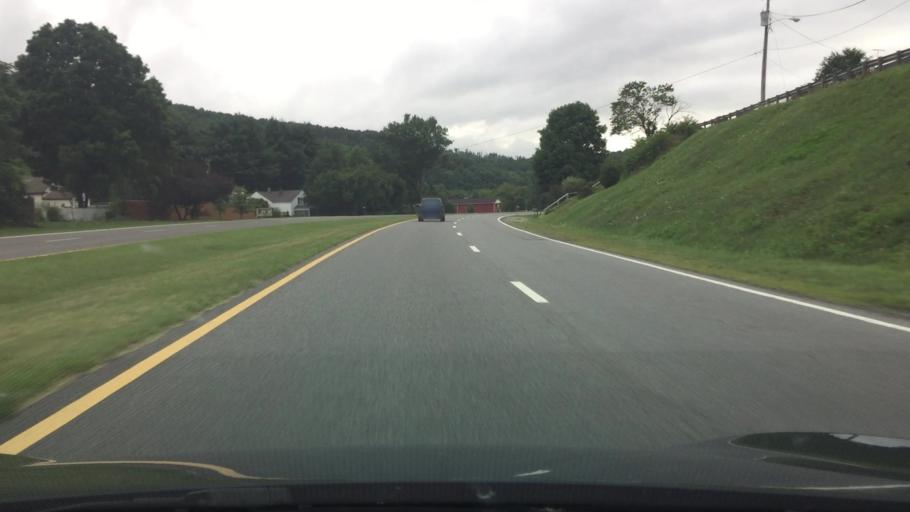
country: US
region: Virginia
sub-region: Montgomery County
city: Shawsville
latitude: 37.2177
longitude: -80.2309
